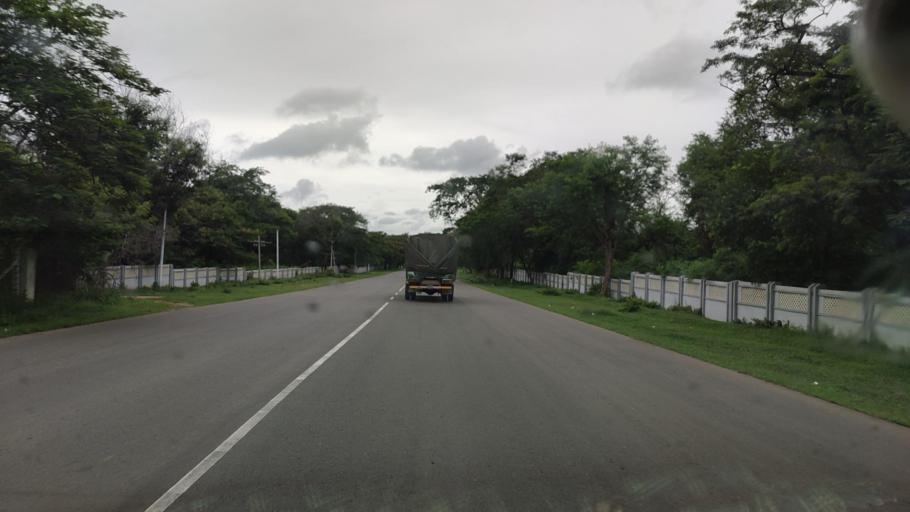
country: MM
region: Mandalay
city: Meiktila
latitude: 20.8452
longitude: 95.8913
